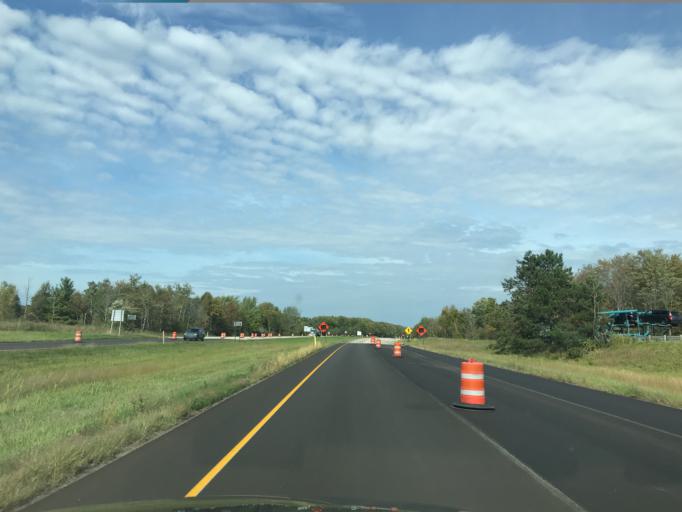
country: US
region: Ohio
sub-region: Ashtabula County
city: Ashtabula
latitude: 41.8088
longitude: -80.7582
